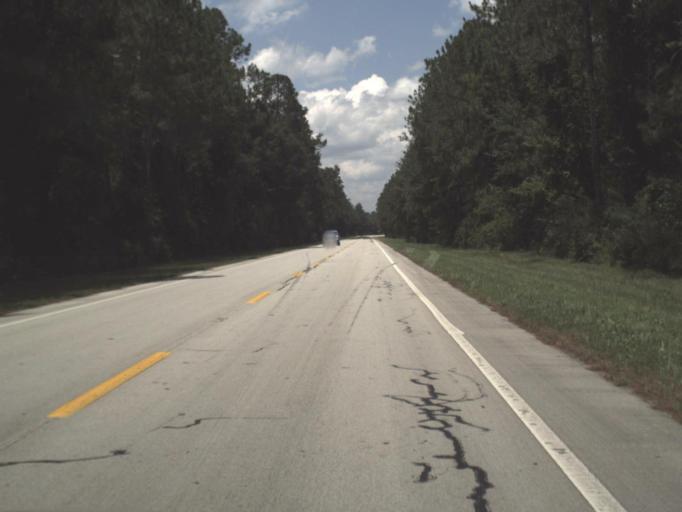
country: US
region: Florida
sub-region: Baker County
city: Macclenny
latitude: 30.1608
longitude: -82.1846
